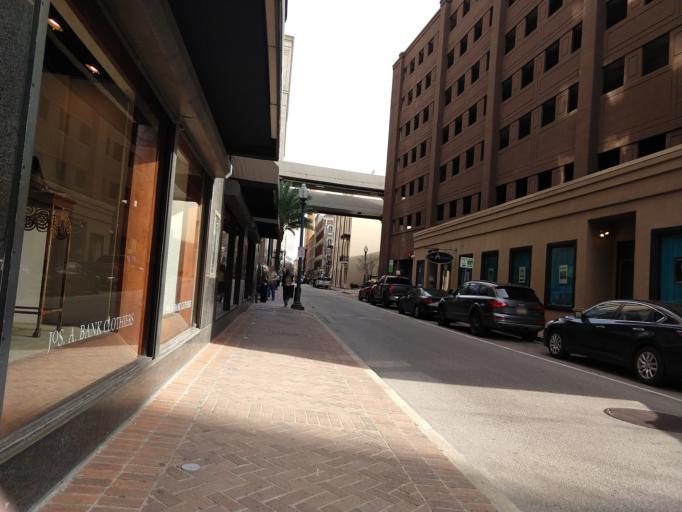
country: US
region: Louisiana
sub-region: Orleans Parish
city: New Orleans
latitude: 29.9521
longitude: -90.0712
